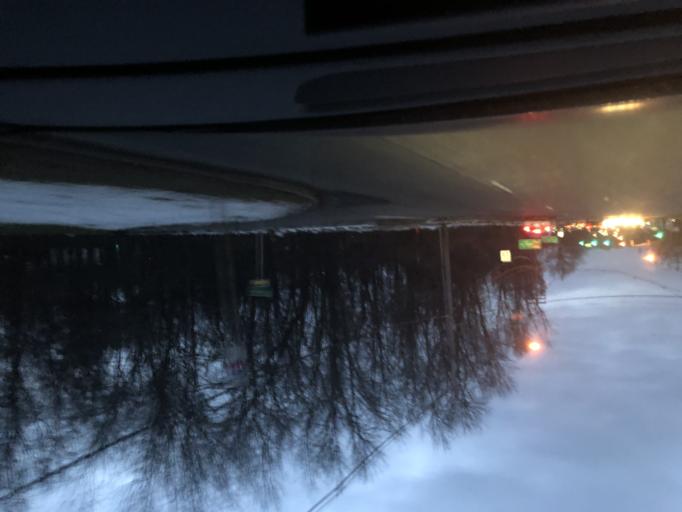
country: US
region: New Jersey
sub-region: Morris County
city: Florham Park
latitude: 40.7891
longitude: -74.3981
